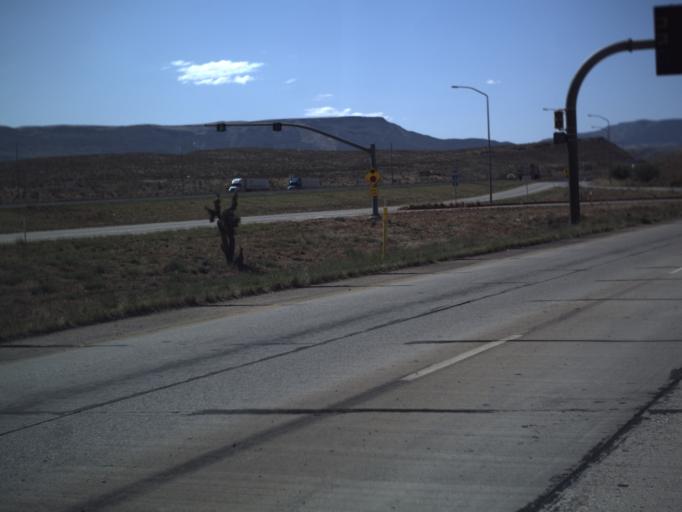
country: US
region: Utah
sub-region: Washington County
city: Saint George
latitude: 37.0124
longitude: -113.6160
